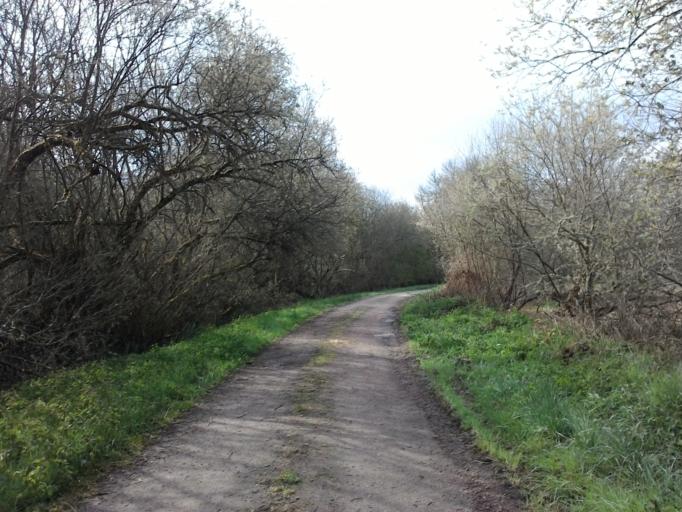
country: FR
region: Bourgogne
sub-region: Departement de la Cote-d'Or
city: Saulieu
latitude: 47.2519
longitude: 4.2086
